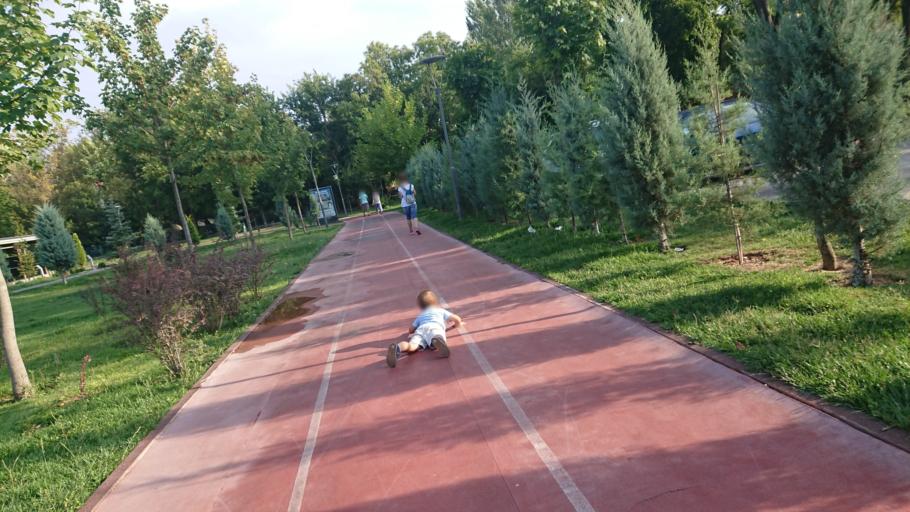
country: TR
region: Eskisehir
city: Eskisehir
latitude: 39.7646
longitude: 30.4945
